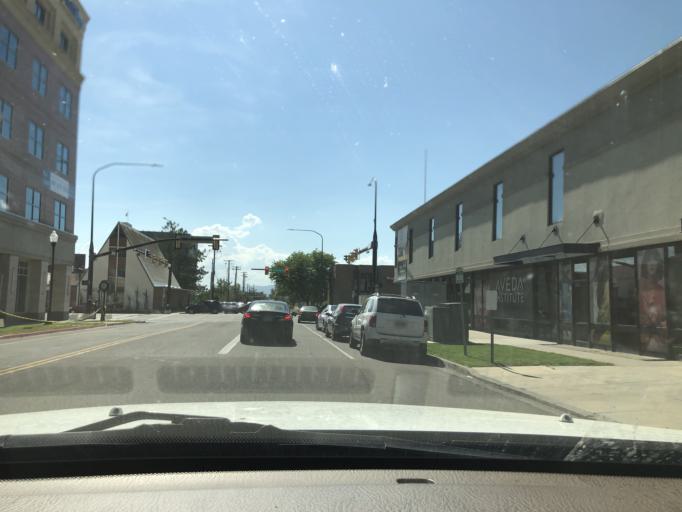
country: US
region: Utah
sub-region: Utah County
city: Provo
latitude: 40.2365
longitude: -111.6579
